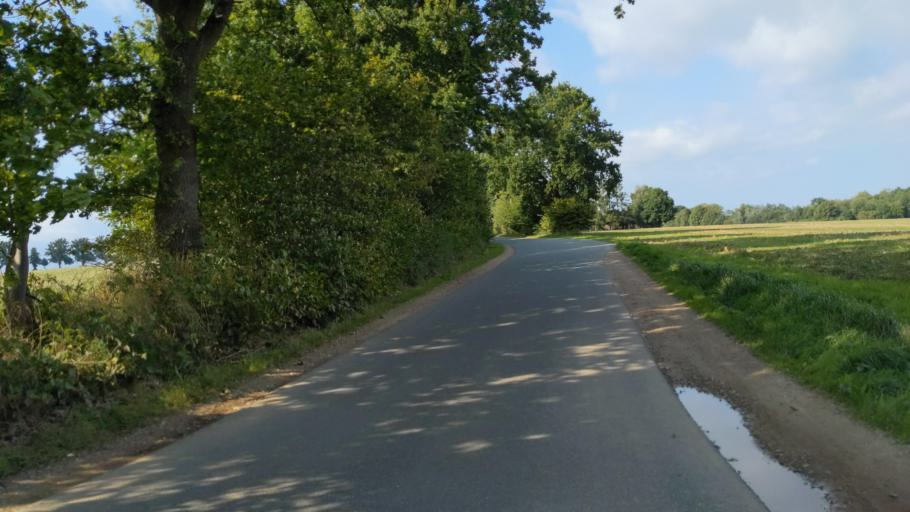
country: DE
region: Mecklenburg-Vorpommern
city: Kalkhorst
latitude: 53.9736
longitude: 11.0101
